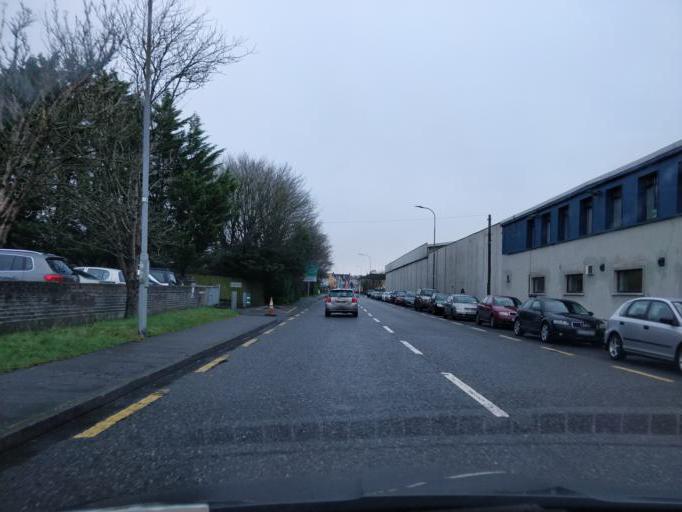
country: IE
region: Connaught
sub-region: Maigh Eo
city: Ballyhaunis
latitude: 53.7599
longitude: -8.7693
